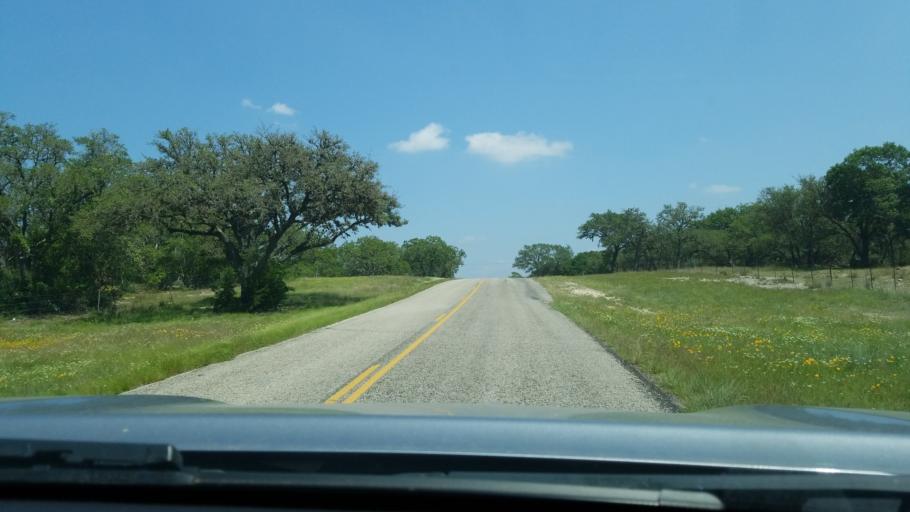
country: US
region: Texas
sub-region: Blanco County
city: Blanco
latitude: 29.9744
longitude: -98.5354
